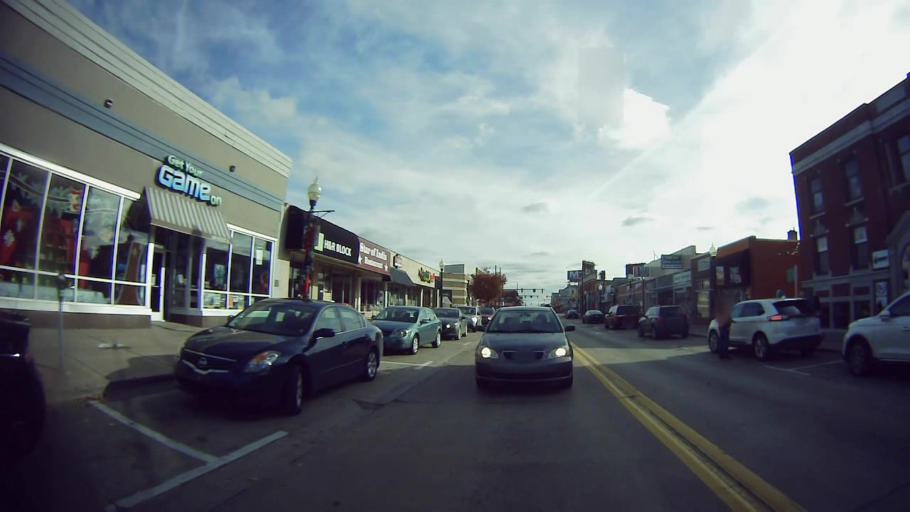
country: US
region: Michigan
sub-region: Oakland County
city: Ferndale
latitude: 42.4606
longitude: -83.1378
